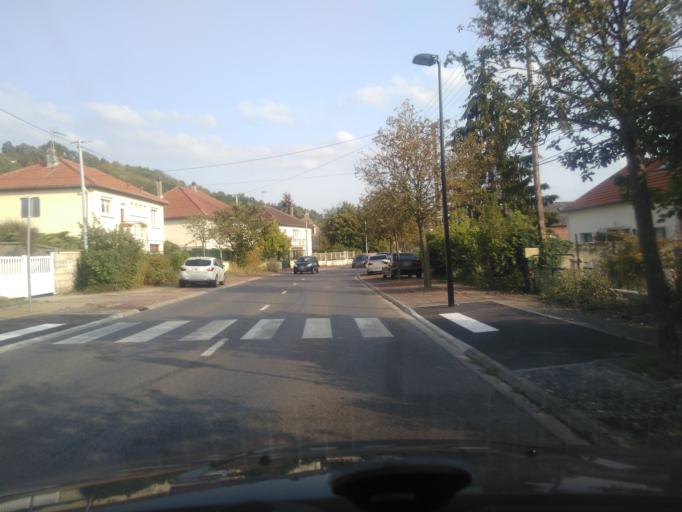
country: FR
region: Picardie
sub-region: Departement de l'Aisne
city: Laon
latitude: 49.5549
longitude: 3.6058
